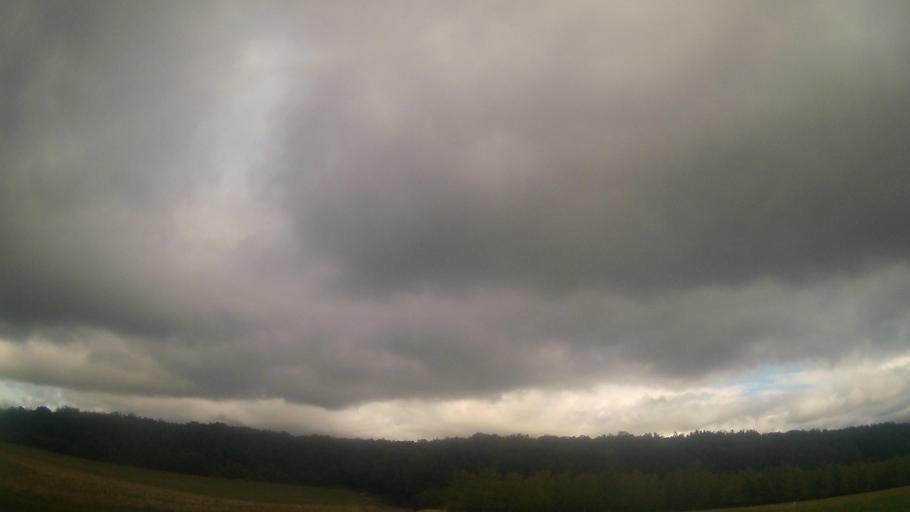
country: DE
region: Rheinland-Pfalz
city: Bornheim
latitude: 49.7698
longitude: 8.0599
